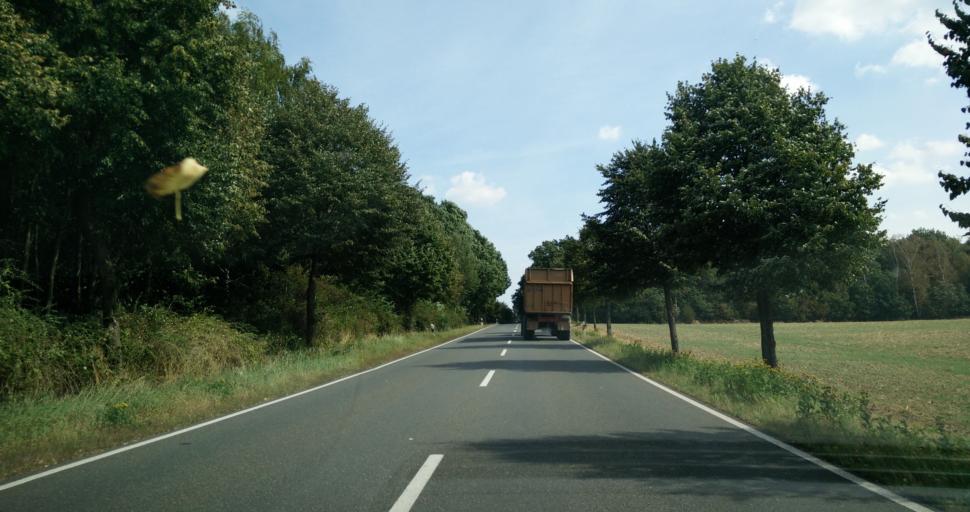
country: DE
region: Saxony
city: Bad Lausick
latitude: 51.1337
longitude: 12.7072
